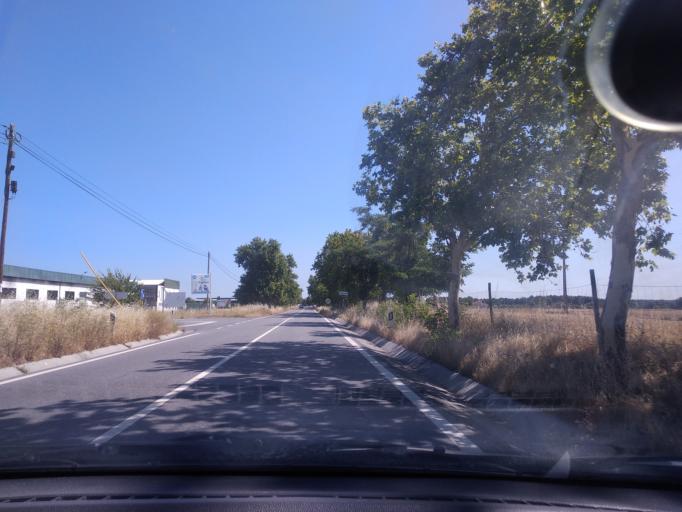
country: PT
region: Guarda
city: Alcains
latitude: 39.9319
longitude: -7.4610
